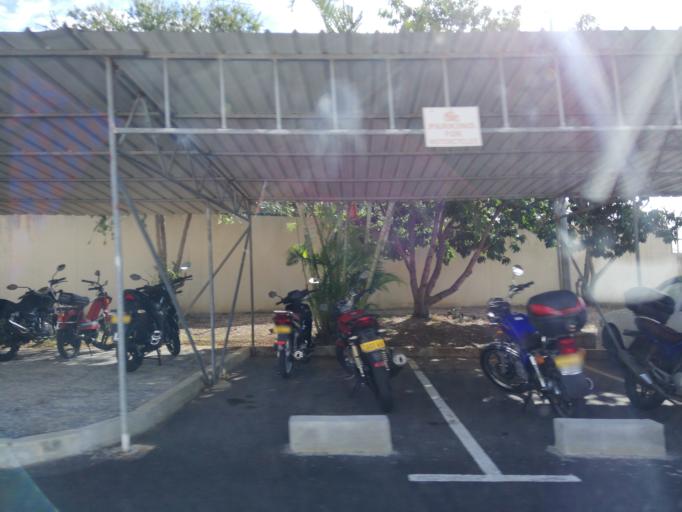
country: MU
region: Plaines Wilhems
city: Ebene
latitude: -20.2279
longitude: 57.4605
